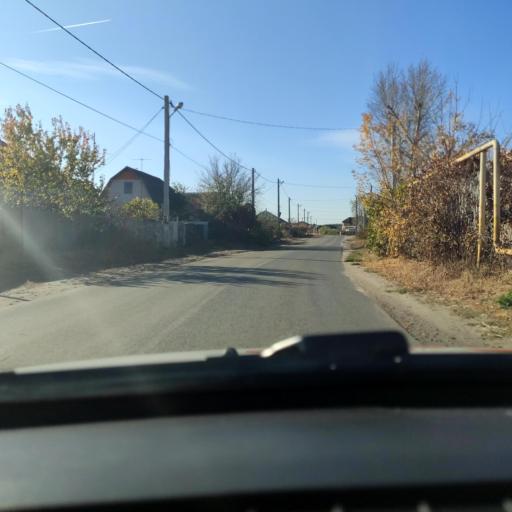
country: RU
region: Voronezj
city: Shilovo
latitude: 51.5236
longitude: 39.1490
